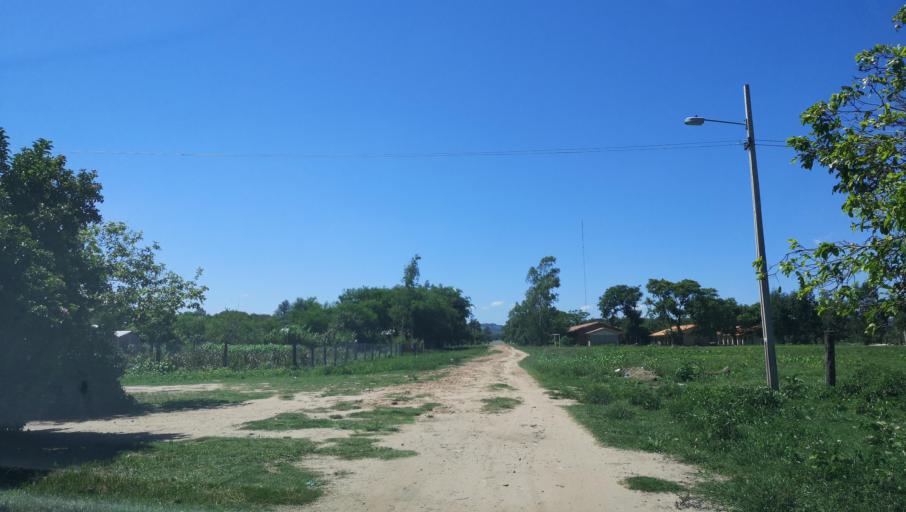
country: PY
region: Caaguazu
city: Carayao
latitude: -25.1960
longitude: -56.4062
